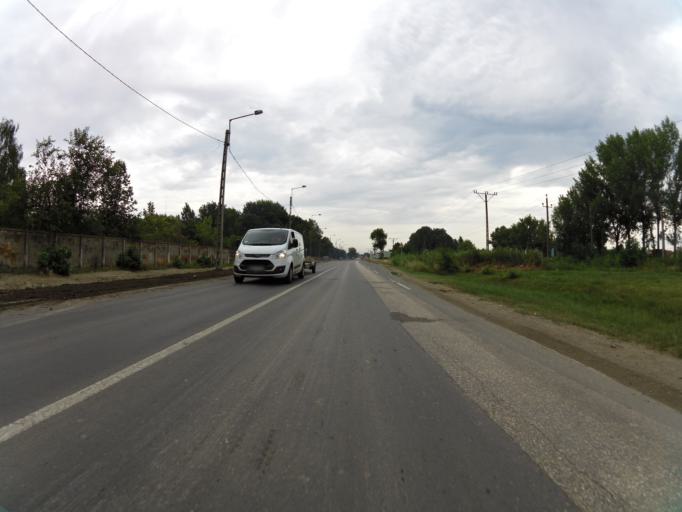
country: HU
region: Csongrad
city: Szeged
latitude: 46.2783
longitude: 20.0967
